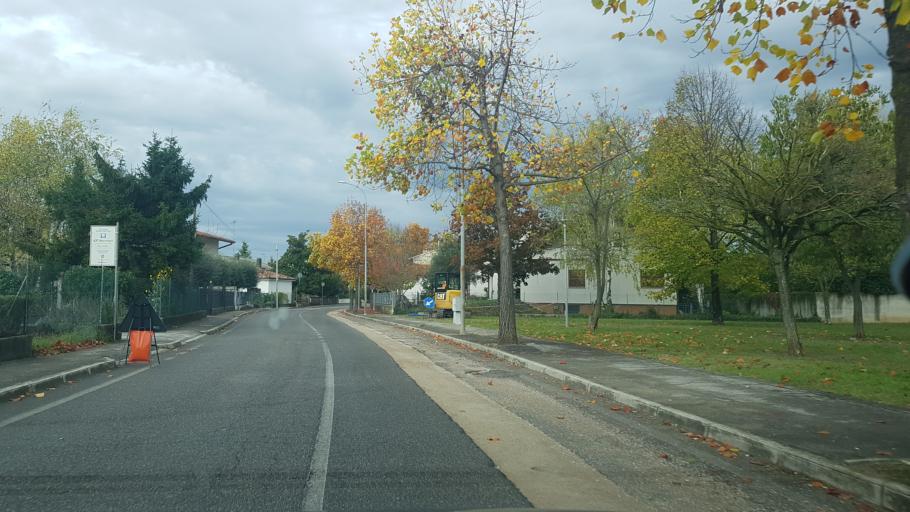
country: IT
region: Friuli Venezia Giulia
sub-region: Provincia di Gorizia
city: Ronchi dei Legionari
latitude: 45.8252
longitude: 13.5131
